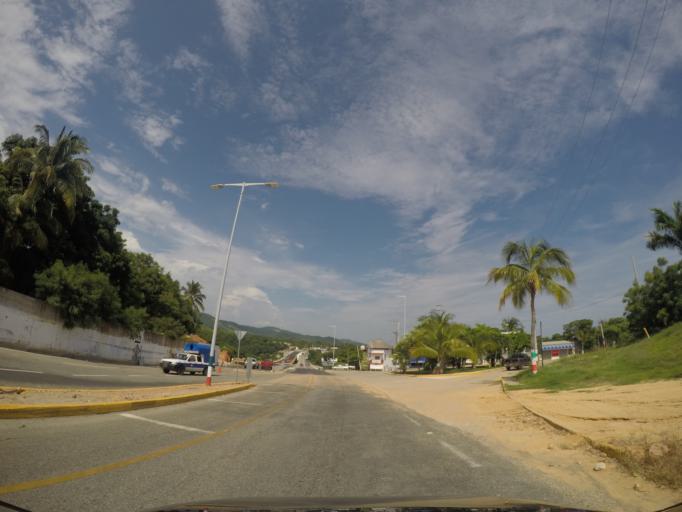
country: MX
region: Oaxaca
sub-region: Santa Maria Colotepec
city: Brisas de Zicatela
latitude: 15.8270
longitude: -97.0288
